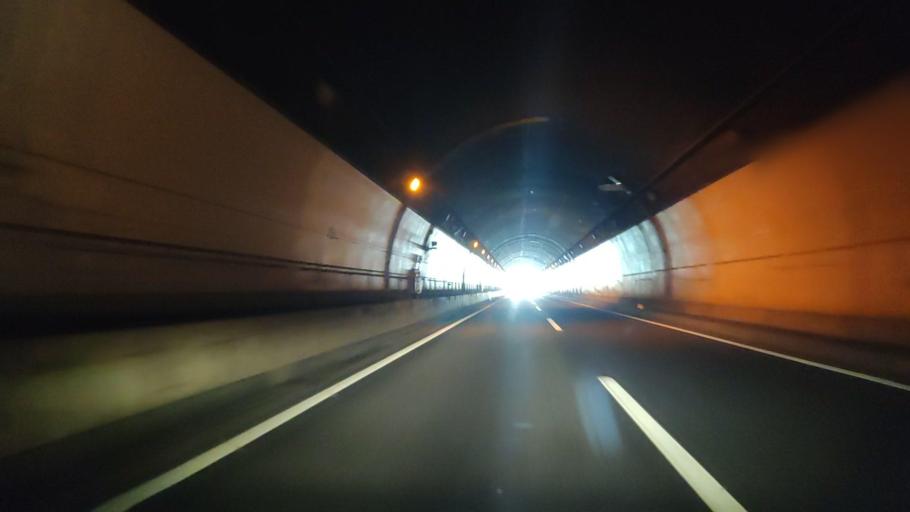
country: JP
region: Akita
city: Hanawa
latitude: 40.0178
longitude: 140.9852
